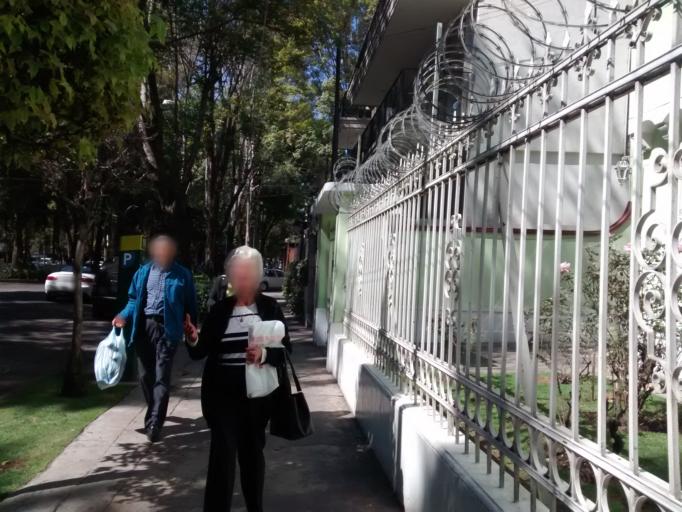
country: MX
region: Mexico City
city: Miguel Hidalgo
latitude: 19.4339
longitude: -99.1929
